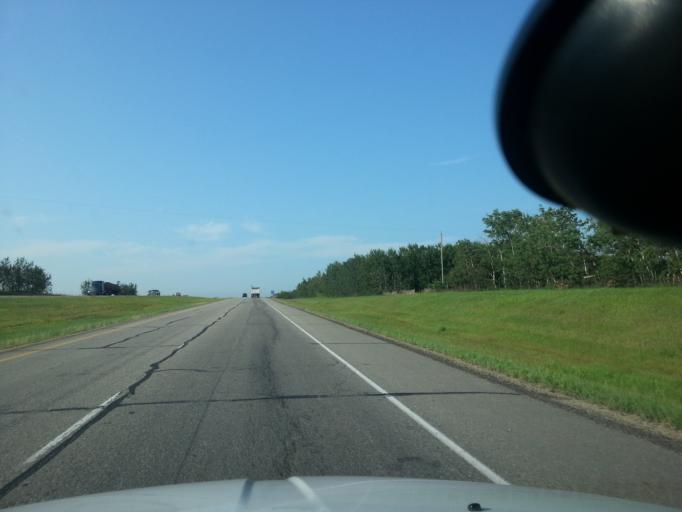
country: CA
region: Alberta
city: Millet
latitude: 53.0479
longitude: -113.6039
